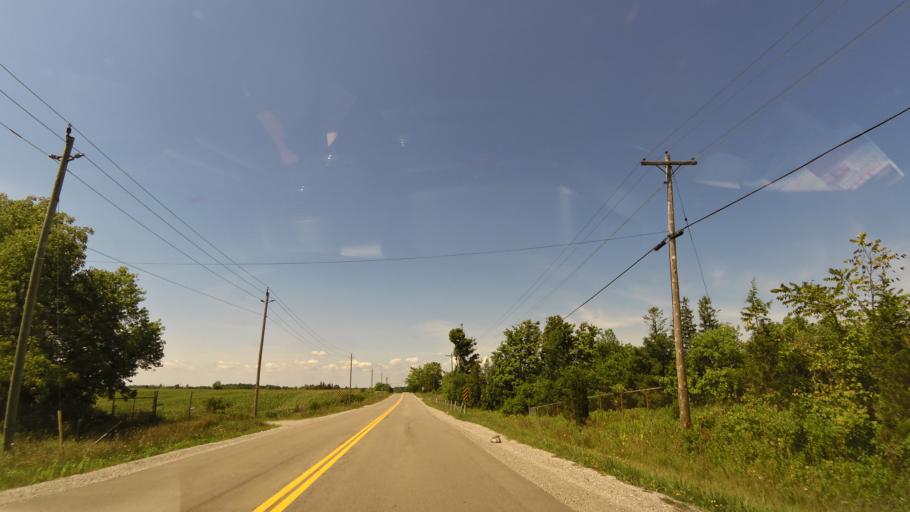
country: CA
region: Ontario
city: Ancaster
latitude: 43.1612
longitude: -79.9357
